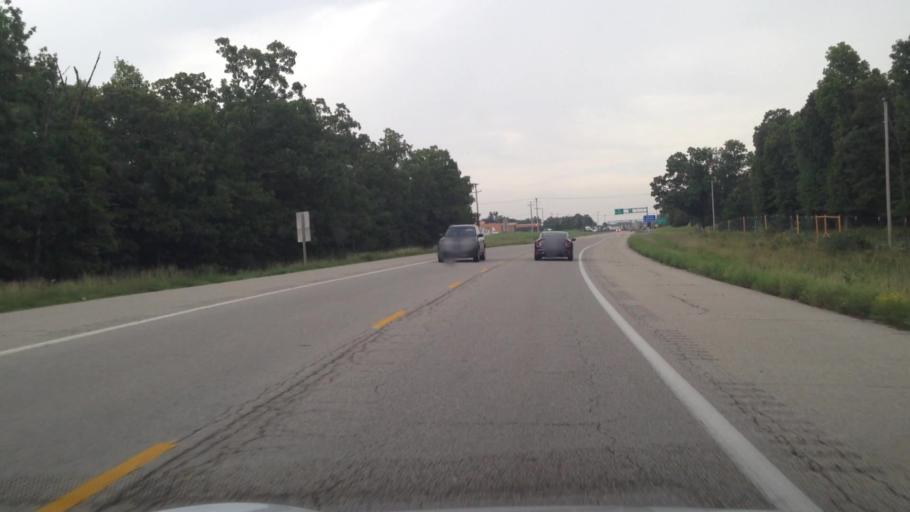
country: US
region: Kansas
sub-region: Cherokee County
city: Galena
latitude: 37.0061
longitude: -94.6192
